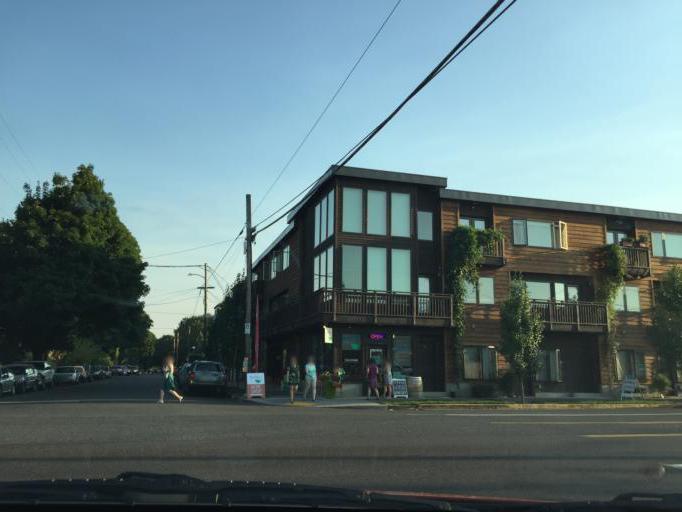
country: US
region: Oregon
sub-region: Multnomah County
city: Portland
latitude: 45.5266
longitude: -122.6414
